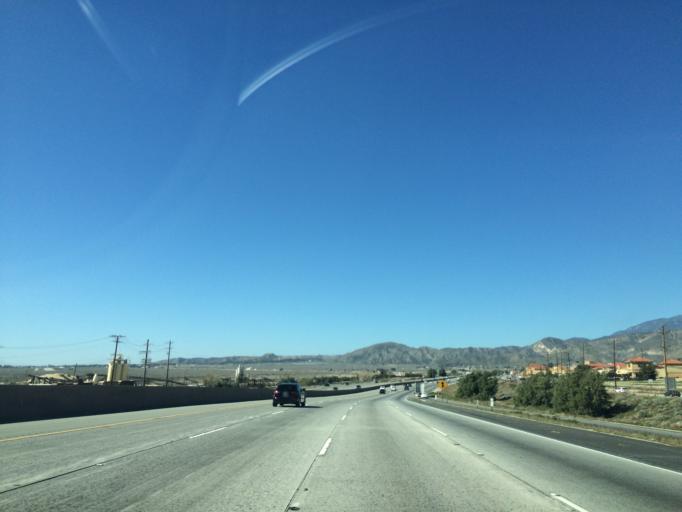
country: US
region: California
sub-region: Riverside County
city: Cabazon
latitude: 33.9218
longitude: -116.8073
